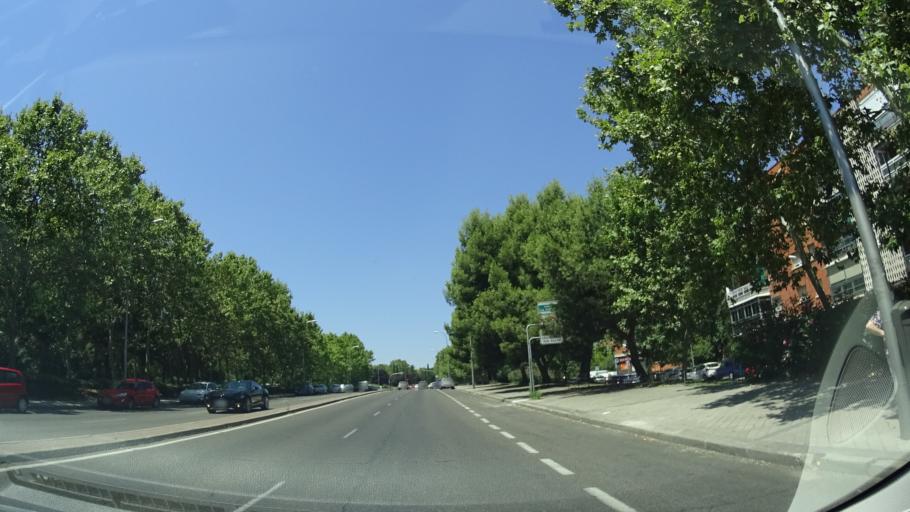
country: ES
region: Madrid
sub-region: Provincia de Madrid
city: Latina
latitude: 40.3766
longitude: -3.7510
